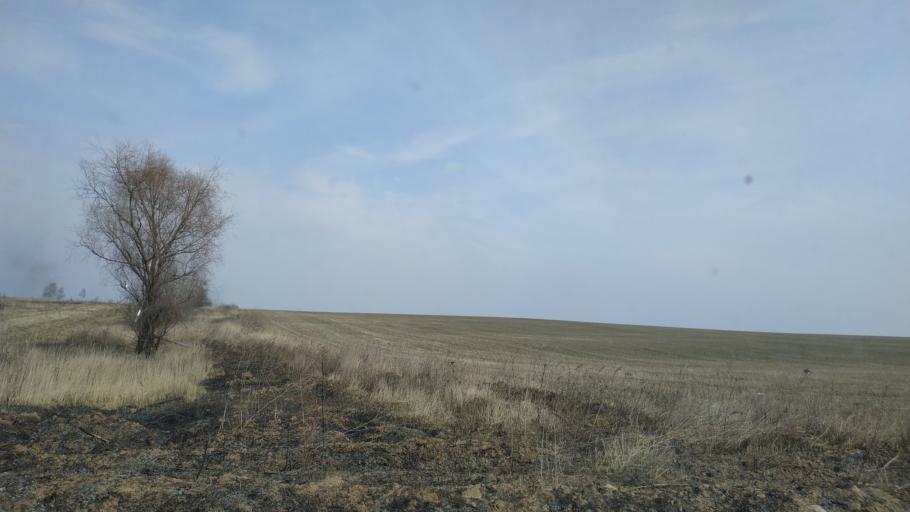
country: RU
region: Moskovskaya
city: Troitskoye
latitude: 55.3580
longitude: 38.4642
